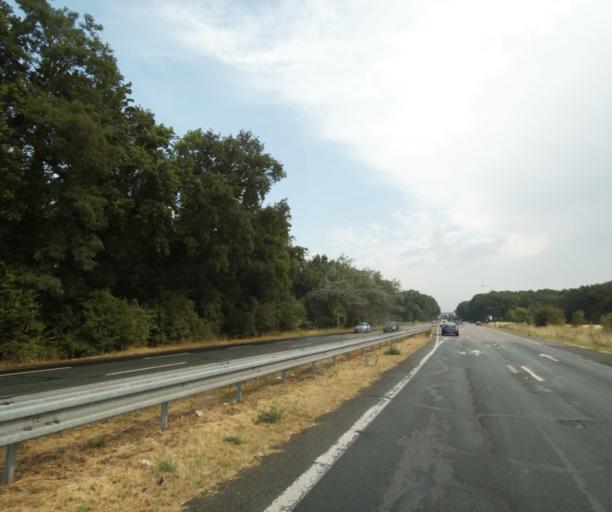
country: FR
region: Ile-de-France
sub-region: Departement du Val-d'Oise
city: Neuville-sur-Oise
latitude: 49.0106
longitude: 2.0744
